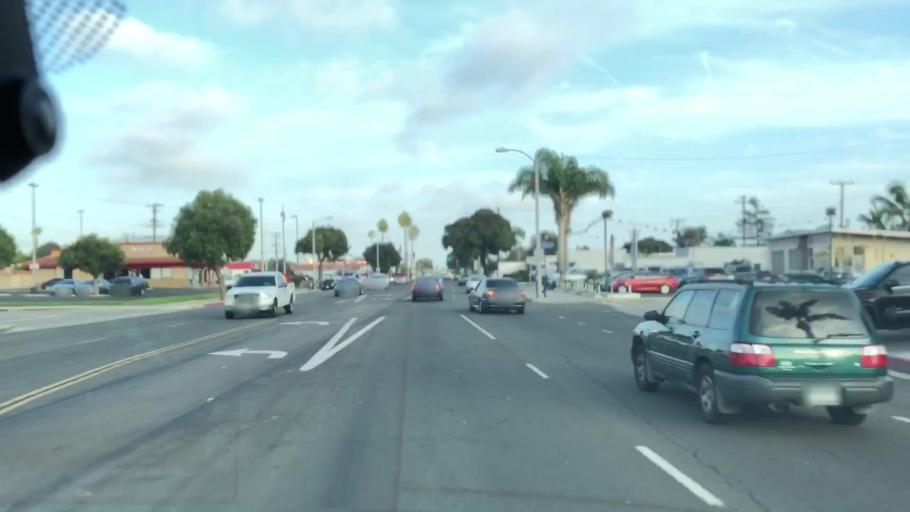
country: US
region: California
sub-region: Ventura County
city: Ventura
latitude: 34.2734
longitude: -119.2656
